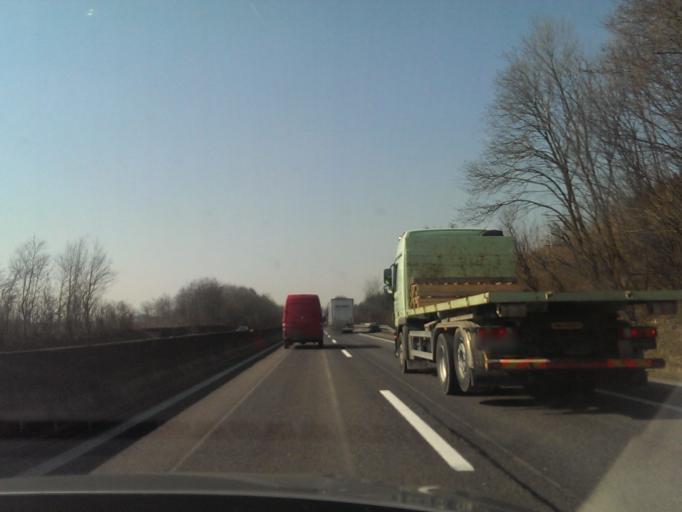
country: AT
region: Upper Austria
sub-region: Politischer Bezirk Ried im Innkreis
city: Ried im Innkreis
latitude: 48.2411
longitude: 13.5552
